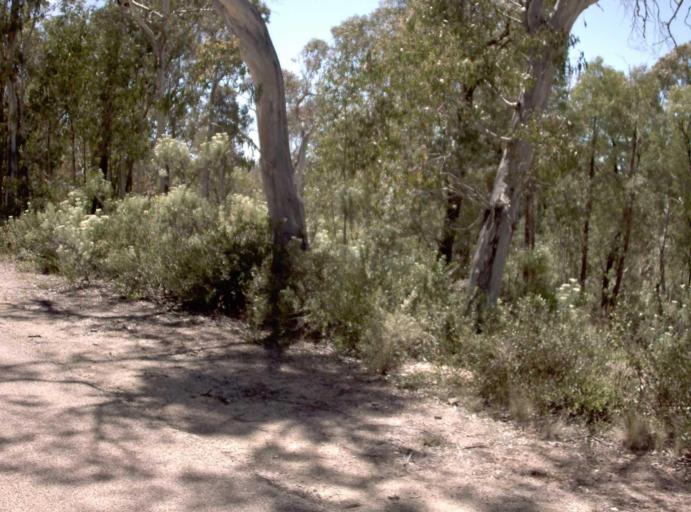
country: AU
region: New South Wales
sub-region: Snowy River
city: Jindabyne
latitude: -37.0434
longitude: 148.2758
